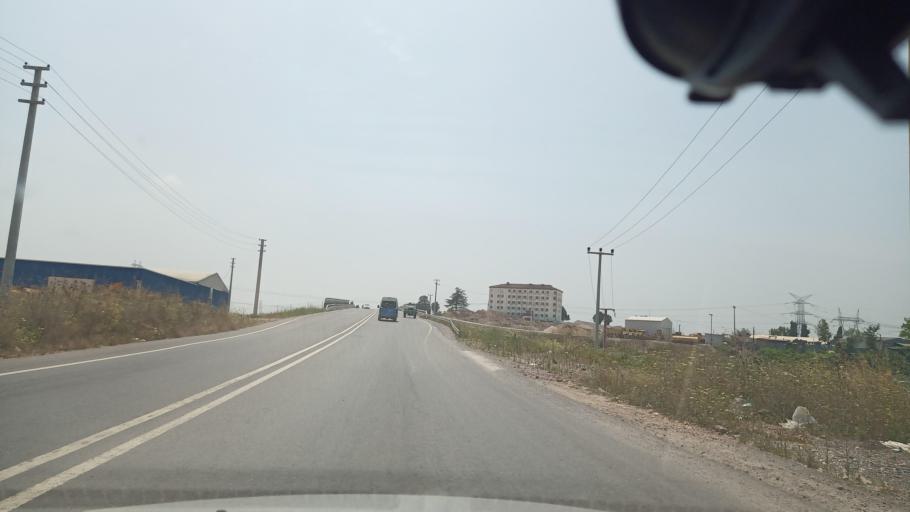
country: TR
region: Sakarya
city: Adapazari
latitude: 40.8264
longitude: 30.3966
